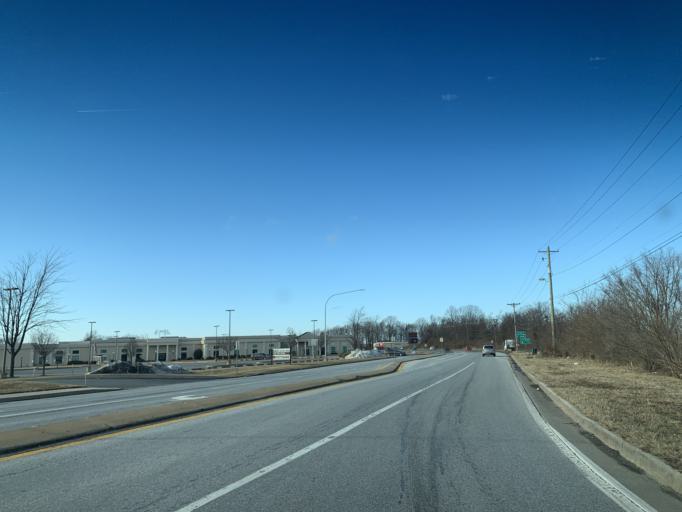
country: US
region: Delaware
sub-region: New Castle County
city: Wilmington Manor
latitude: 39.6657
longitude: -75.6109
